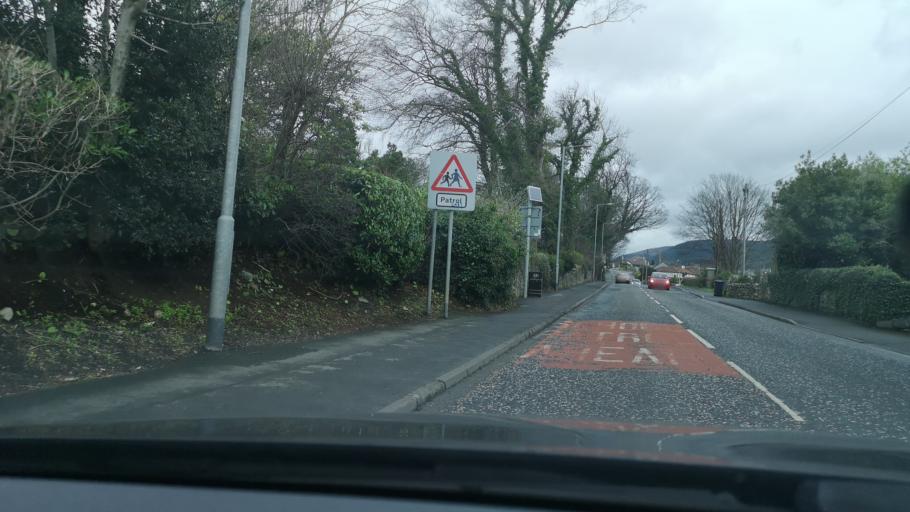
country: GB
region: Northern Ireland
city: Rostrevor
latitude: 54.1042
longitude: -6.1926
